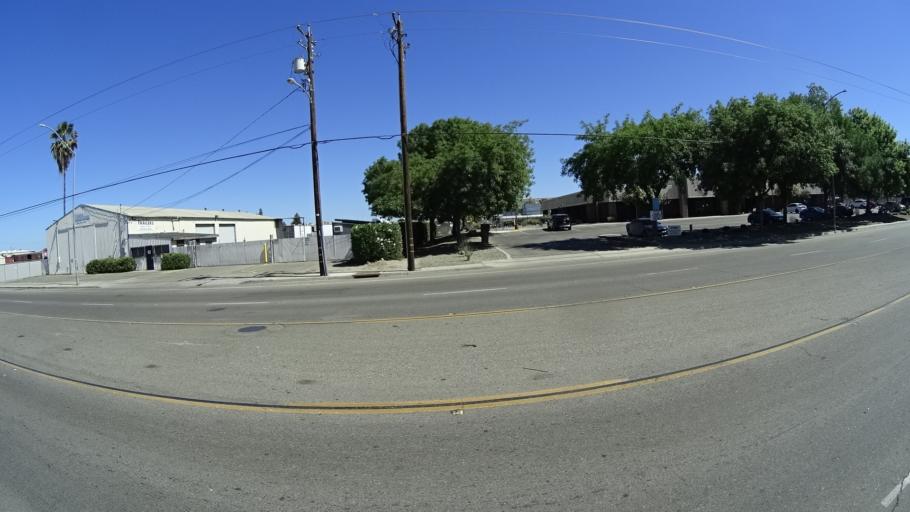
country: US
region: California
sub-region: Fresno County
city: Easton
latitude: 36.6922
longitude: -119.7704
